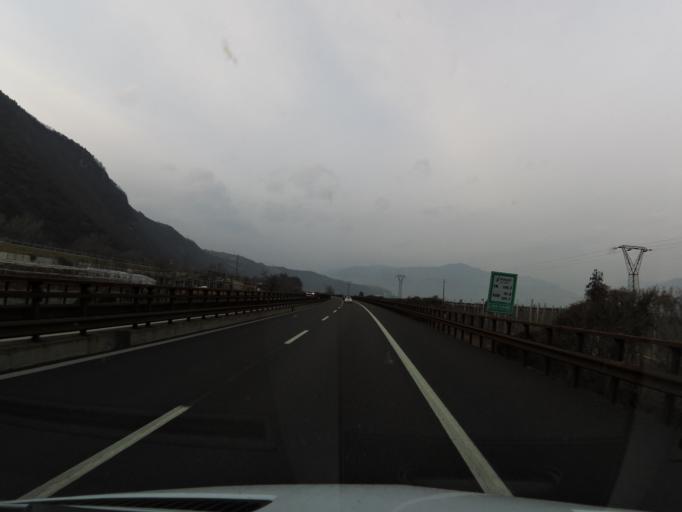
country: IT
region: Trentino-Alto Adige
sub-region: Bolzano
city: San Giacomo
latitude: 46.4403
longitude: 11.3167
